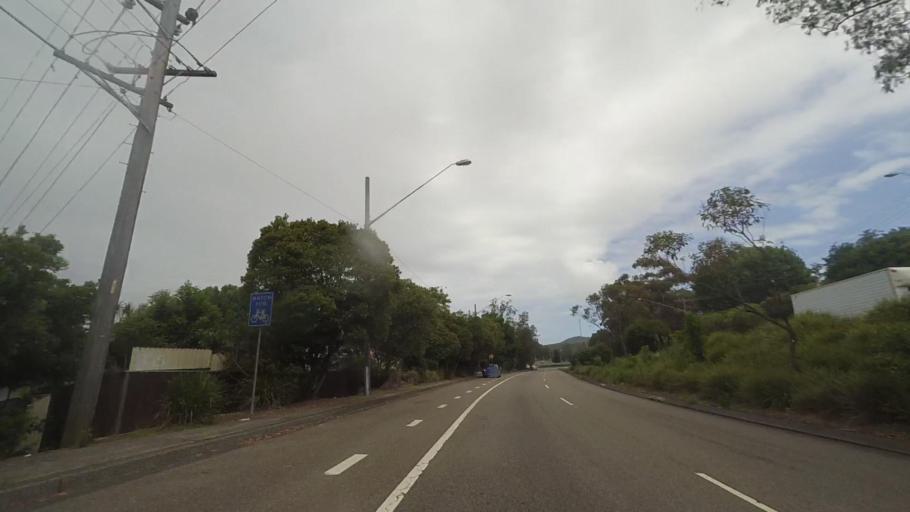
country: AU
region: New South Wales
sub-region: Wyong Shire
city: Berkeley Vale
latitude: -33.3557
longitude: 151.4397
